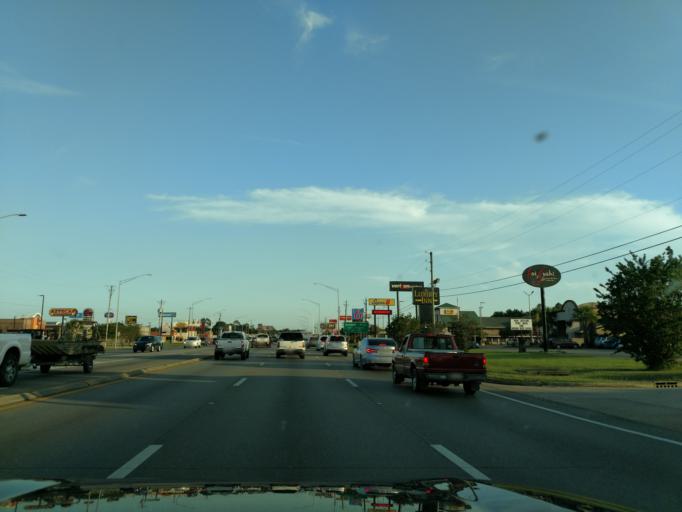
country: US
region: Mississippi
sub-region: Harrison County
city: West Gulfport
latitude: 30.4246
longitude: -89.0926
